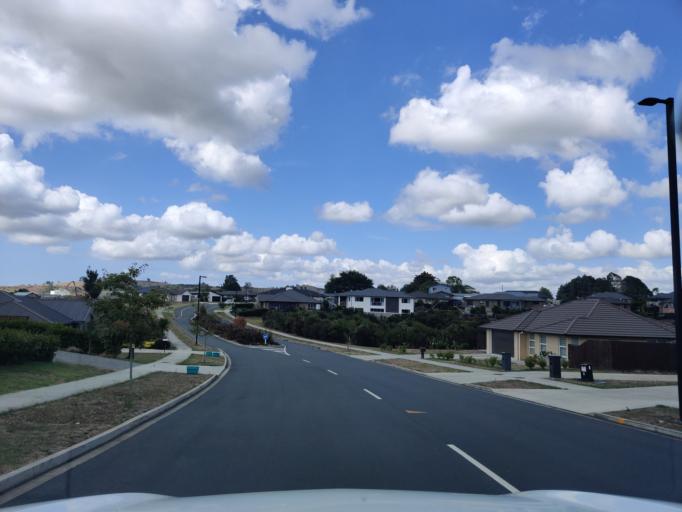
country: NZ
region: Auckland
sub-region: Auckland
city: Pukekohe East
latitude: -37.2401
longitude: 175.0161
